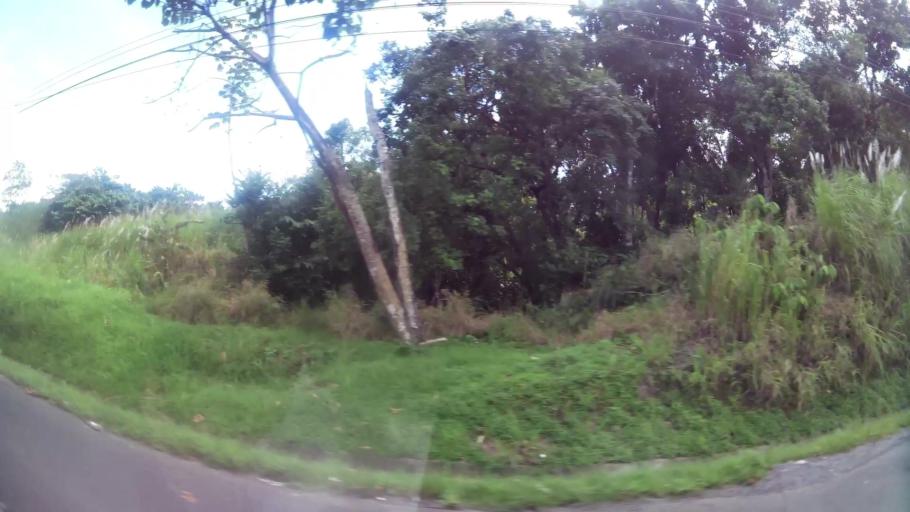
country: PA
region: Panama
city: Las Cumbres
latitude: 9.0410
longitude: -79.5631
